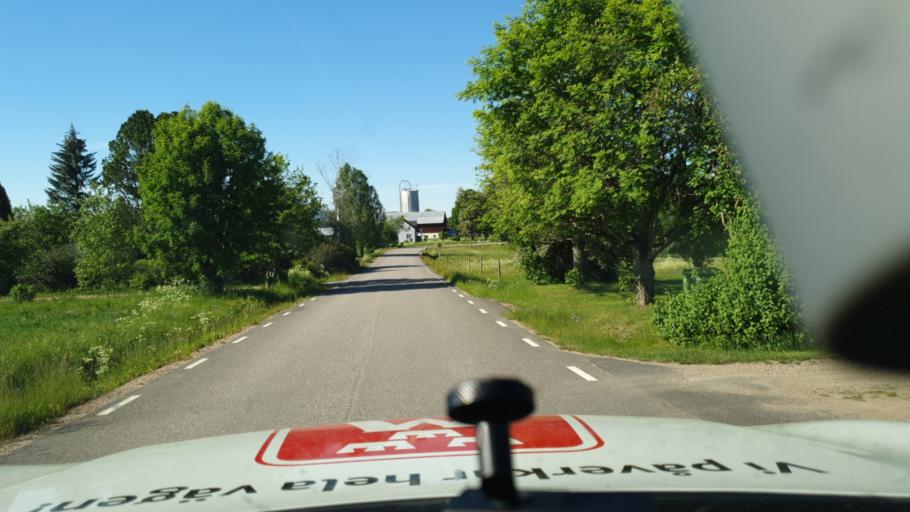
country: SE
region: Vaermland
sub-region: Torsby Kommun
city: Torsby
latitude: 60.1728
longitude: 13.0319
